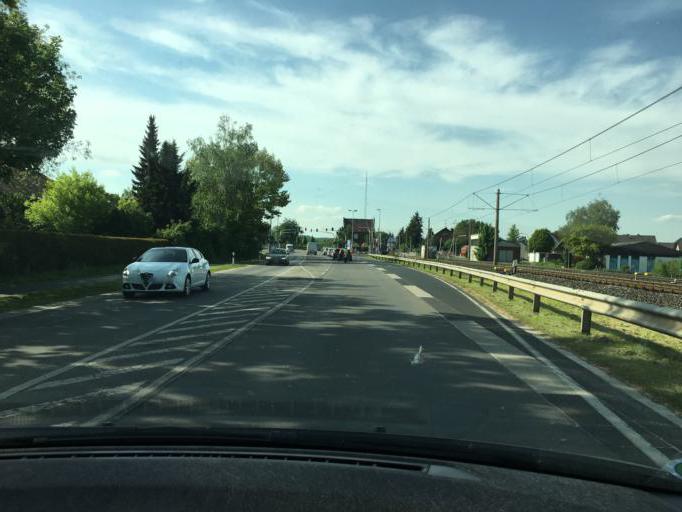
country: DE
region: North Rhine-Westphalia
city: Bruhl
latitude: 50.7994
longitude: 6.9159
